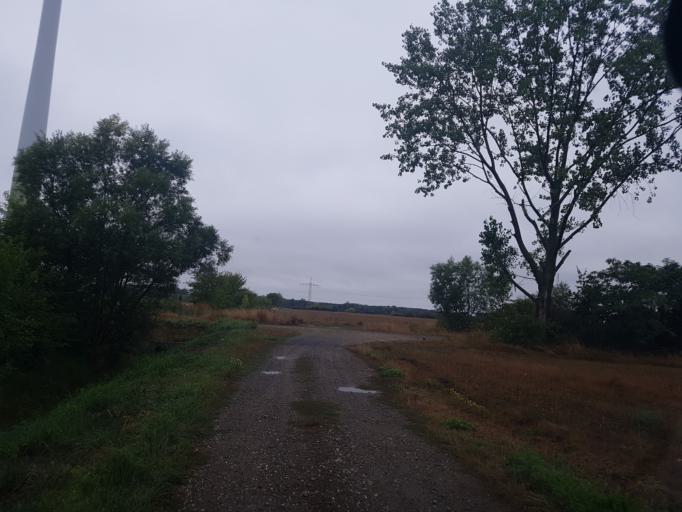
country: DE
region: Brandenburg
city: Merzdorf
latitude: 51.4172
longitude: 13.5095
